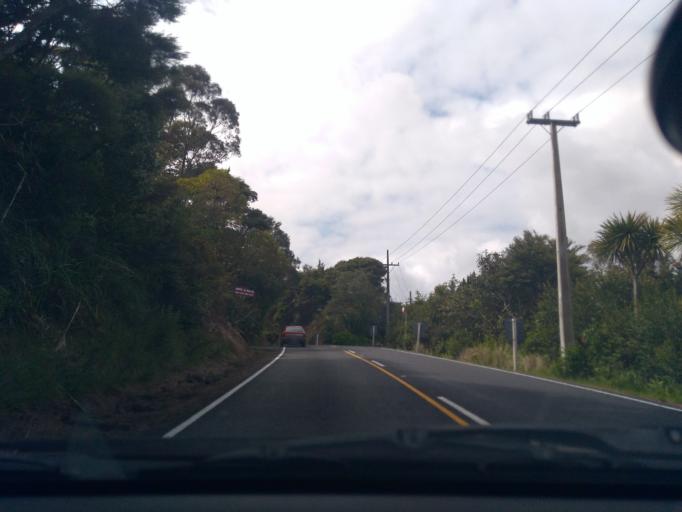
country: NZ
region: Auckland
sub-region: Auckland
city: Muriwai Beach
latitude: -36.8608
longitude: 174.5550
